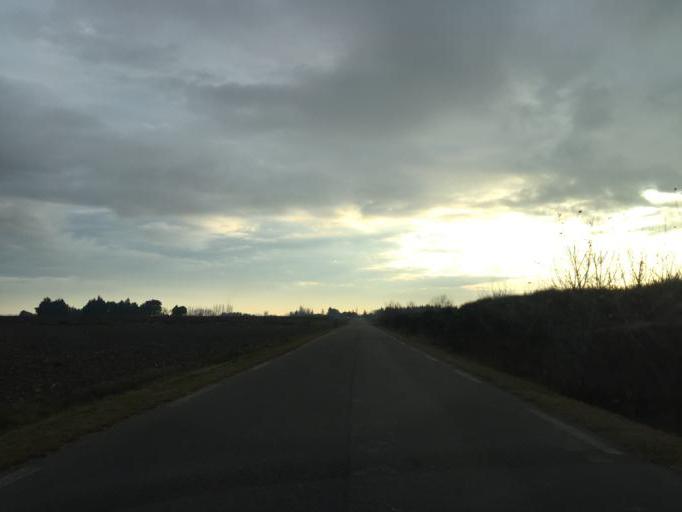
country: FR
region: Provence-Alpes-Cote d'Azur
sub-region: Departement du Vaucluse
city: Jonquieres
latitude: 44.1262
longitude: 4.8684
